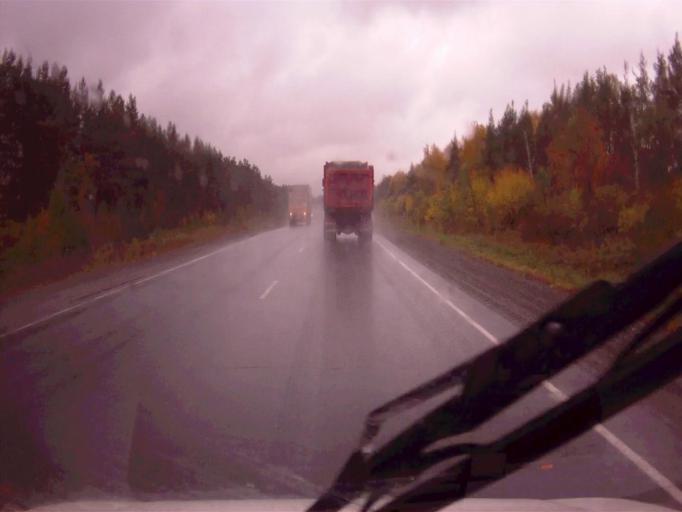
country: RU
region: Chelyabinsk
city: Roshchino
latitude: 55.3569
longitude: 61.2467
